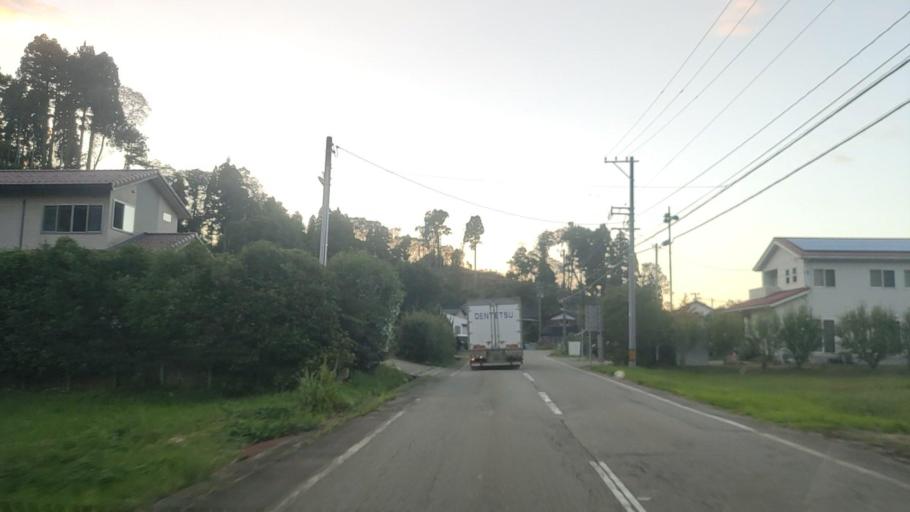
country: JP
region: Ishikawa
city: Tsubata
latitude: 36.6458
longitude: 136.7637
